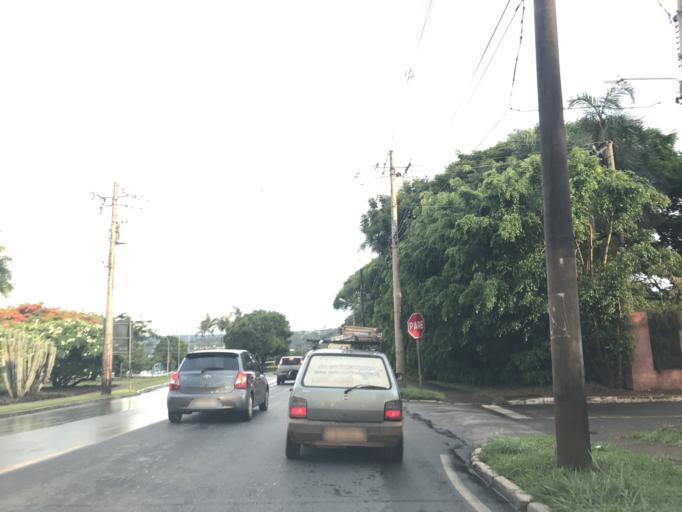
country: BR
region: Federal District
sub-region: Brasilia
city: Brasilia
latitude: -15.8538
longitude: -47.8782
